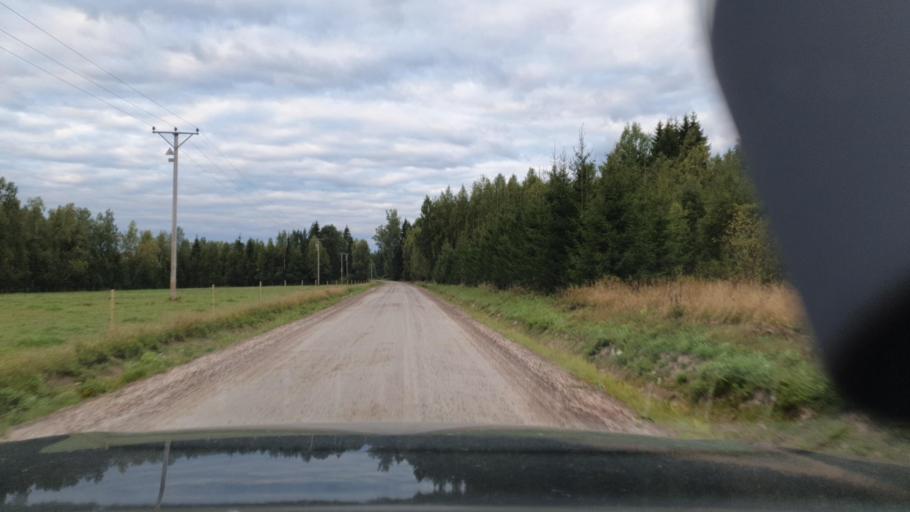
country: SE
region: Vaermland
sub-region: Munkfors Kommun
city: Munkfors
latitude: 59.8960
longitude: 13.5189
